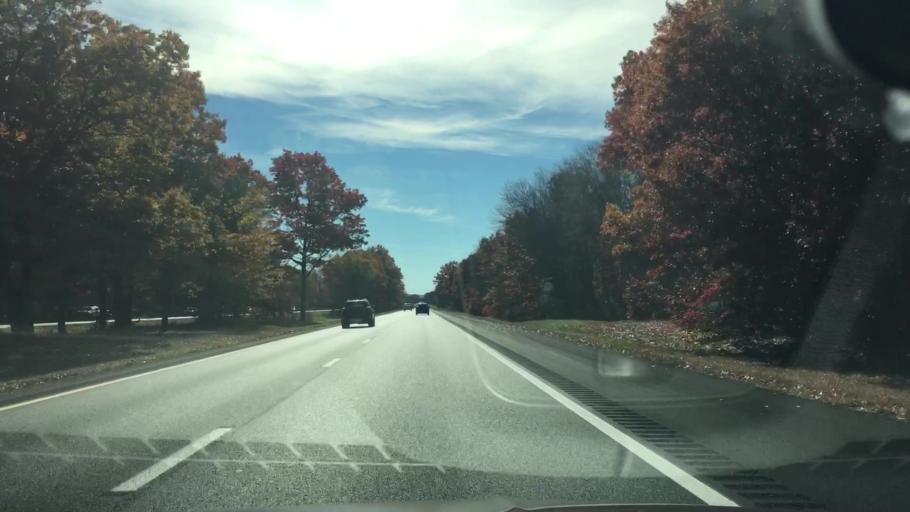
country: US
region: Massachusetts
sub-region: Franklin County
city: Whately
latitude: 42.4241
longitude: -72.6239
